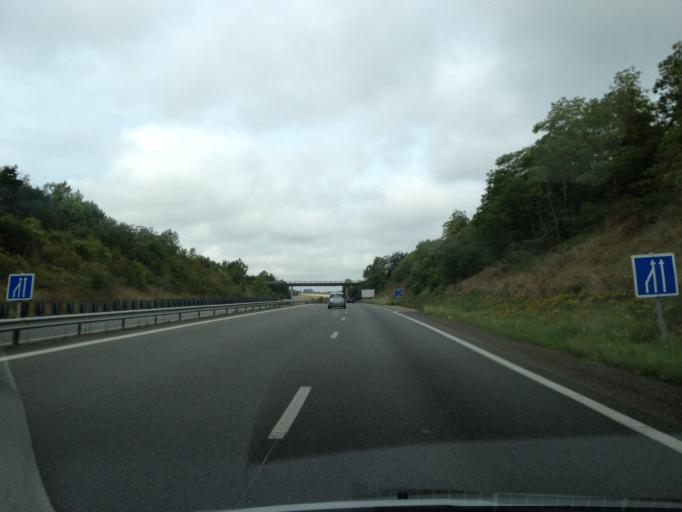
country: FR
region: Midi-Pyrenees
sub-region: Departement du Tarn-et-Garonne
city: Auvillar
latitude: 44.0599
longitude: 0.9069
